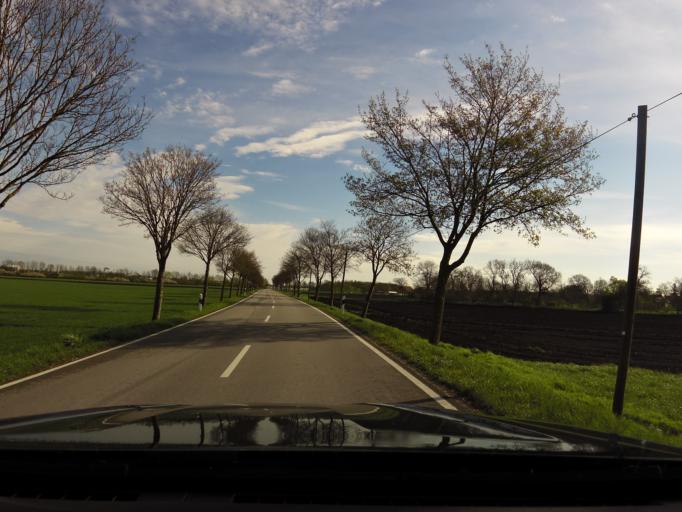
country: DE
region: Bavaria
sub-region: Upper Bavaria
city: Hallbergmoos
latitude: 48.3365
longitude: 11.7892
